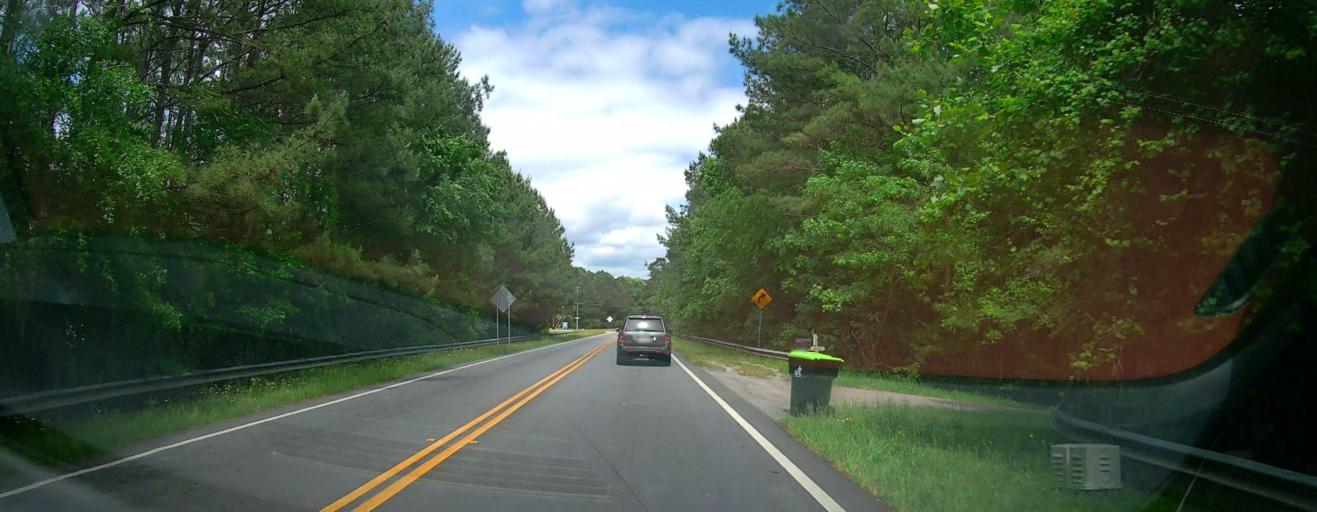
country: US
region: Georgia
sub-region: DeKalb County
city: Pine Mountain
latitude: 33.6197
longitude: -84.0777
